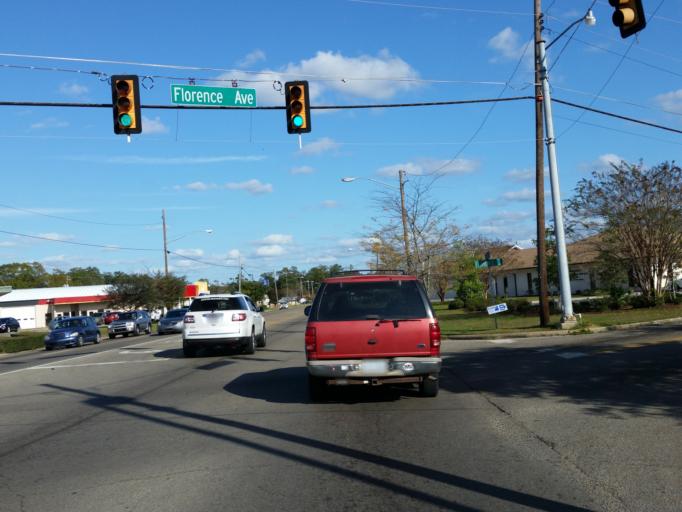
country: US
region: Mississippi
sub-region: Forrest County
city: Hattiesburg
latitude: 31.3161
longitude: -89.3057
